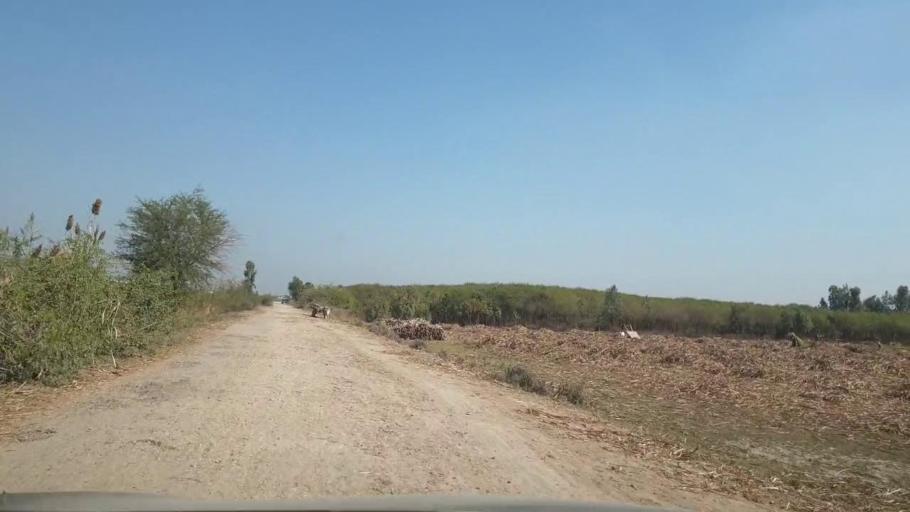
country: PK
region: Sindh
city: Tando Adam
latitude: 25.6272
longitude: 68.6472
